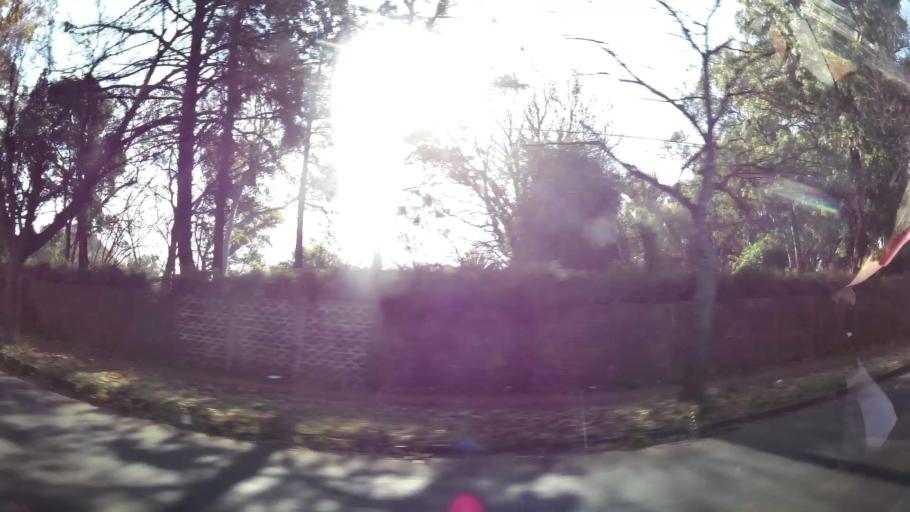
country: ZA
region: Gauteng
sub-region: West Rand District Municipality
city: Randfontein
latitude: -26.1729
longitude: 27.6966
